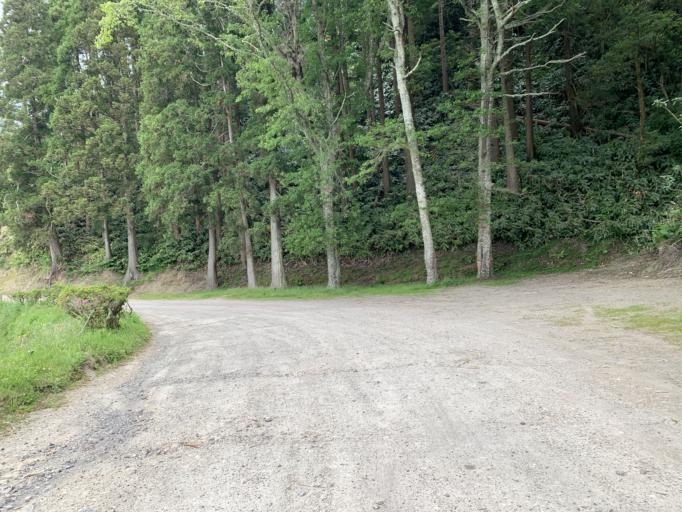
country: PT
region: Azores
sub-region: Ponta Delgada
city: Arrifes
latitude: 37.8522
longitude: -25.7857
